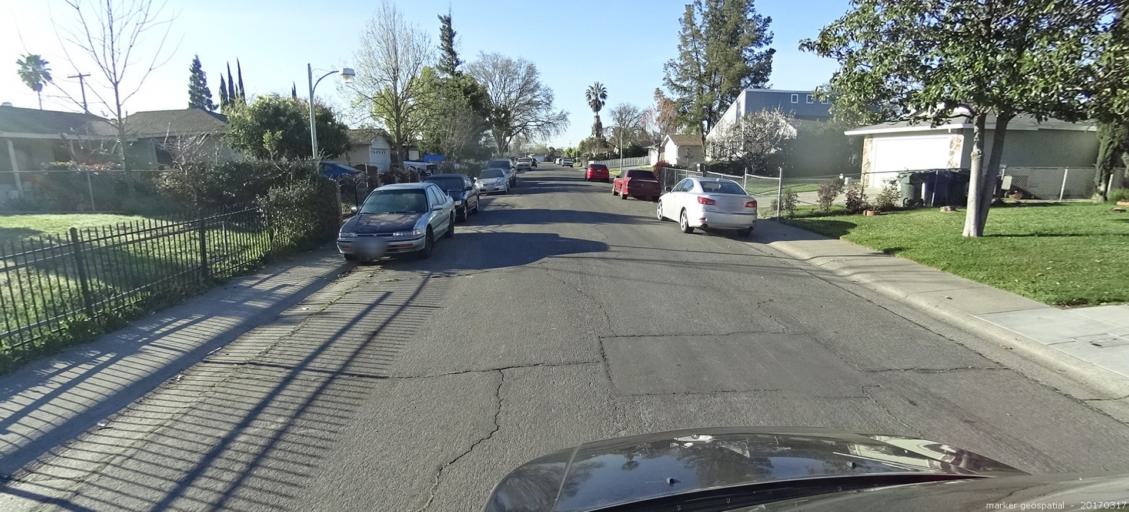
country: US
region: California
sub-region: Sacramento County
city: Parkway
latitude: 38.4852
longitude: -121.4898
